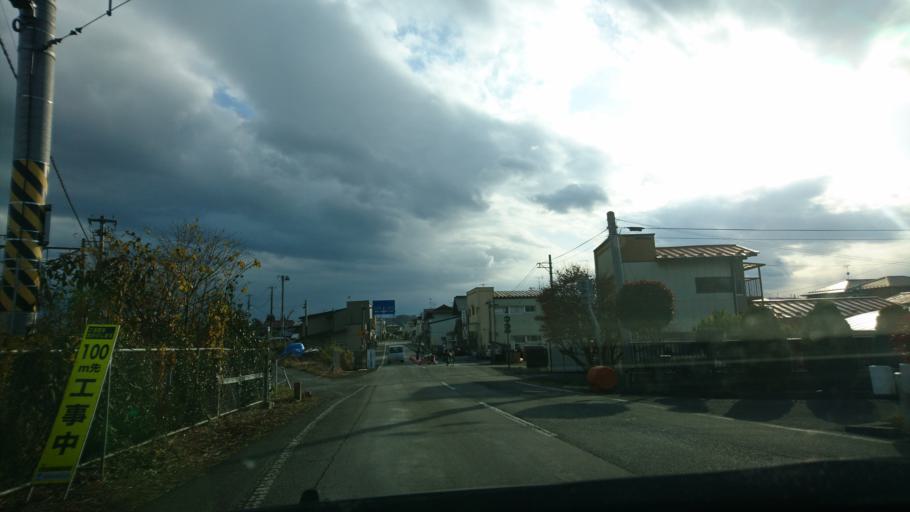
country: JP
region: Iwate
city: Ichinoseki
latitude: 38.9898
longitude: 141.1170
